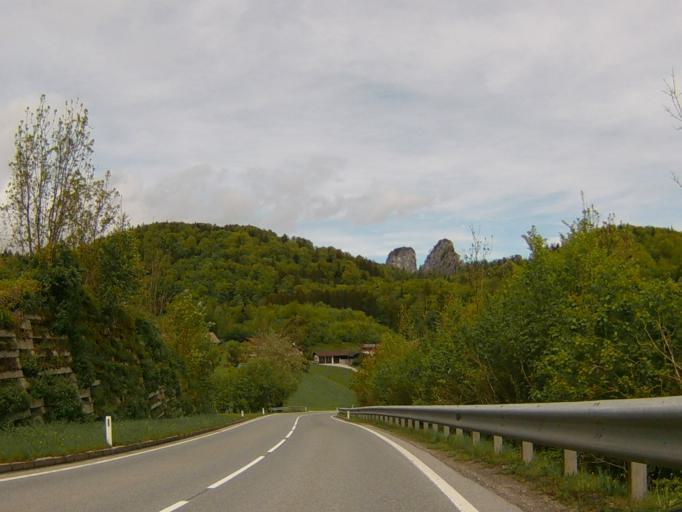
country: AT
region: Salzburg
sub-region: Politischer Bezirk Hallein
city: Hallein
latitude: 47.6746
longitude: 13.0836
